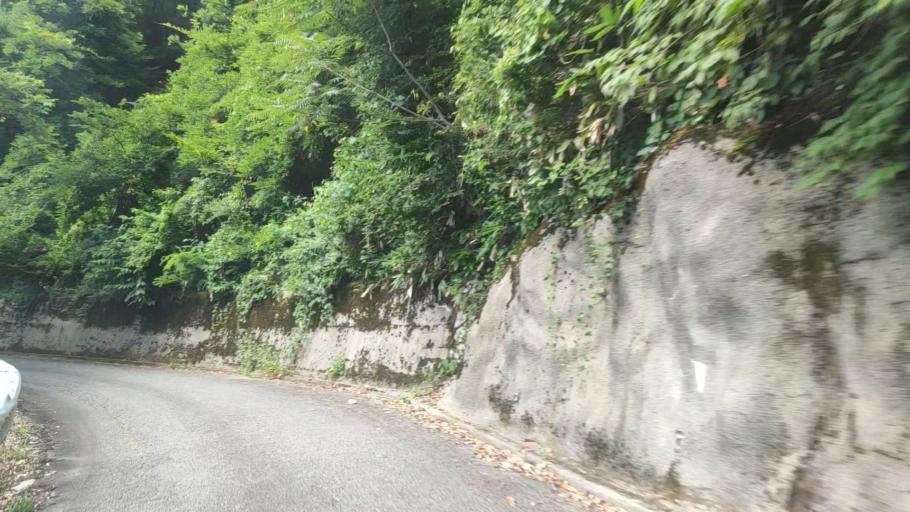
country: JP
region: Ishikawa
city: Komatsu
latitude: 36.2854
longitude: 136.5273
